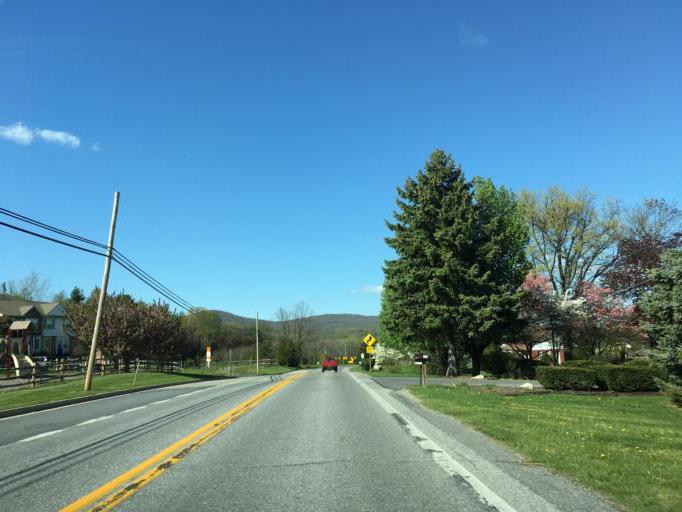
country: US
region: Maryland
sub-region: Frederick County
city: Thurmont
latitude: 39.6360
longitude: -77.4055
